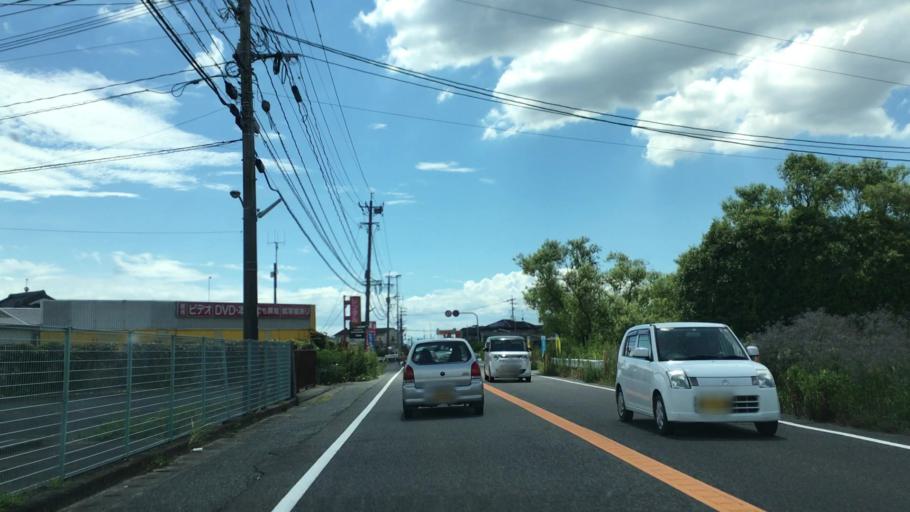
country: JP
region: Saga Prefecture
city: Kanzakimachi-kanzaki
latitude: 33.2891
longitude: 130.3524
